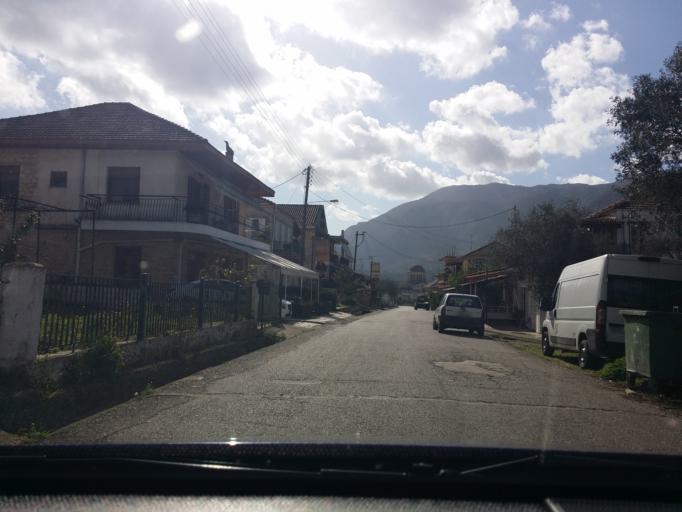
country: GR
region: West Greece
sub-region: Nomos Aitolias kai Akarnanias
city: Astakos
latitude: 38.5948
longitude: 21.0899
